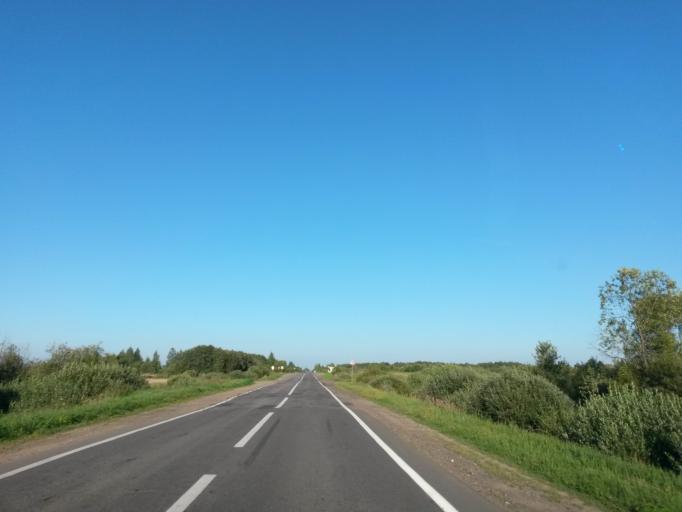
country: RU
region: Jaroslavl
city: Gavrilov-Yam
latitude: 57.3076
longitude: 39.8902
